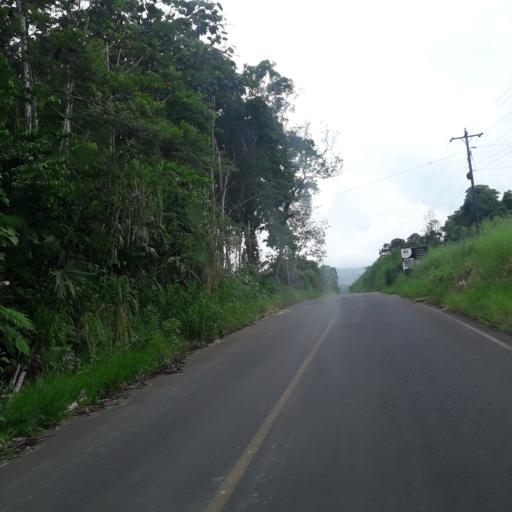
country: EC
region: Napo
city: Tena
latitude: -1.0505
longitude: -77.6636
